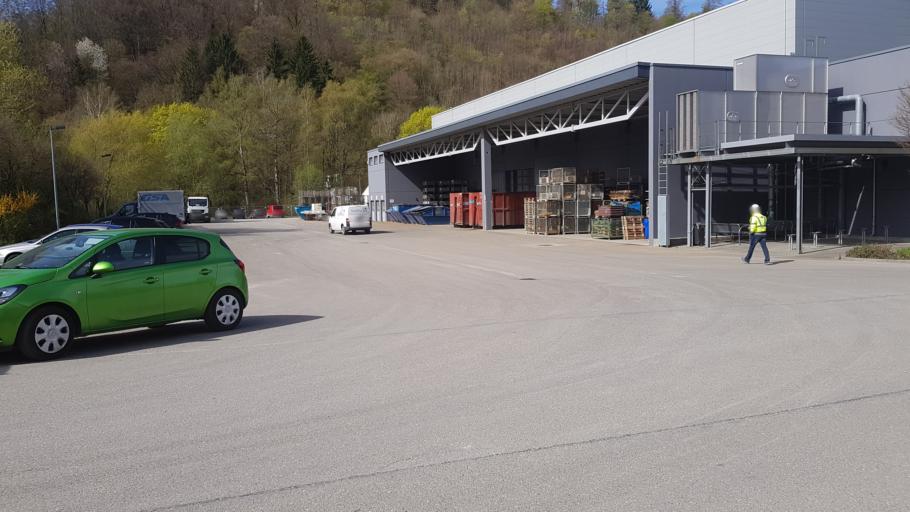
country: DE
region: Baden-Wuerttemberg
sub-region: Regierungsbezirk Stuttgart
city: Aalen
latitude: 48.8180
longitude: 10.1228
